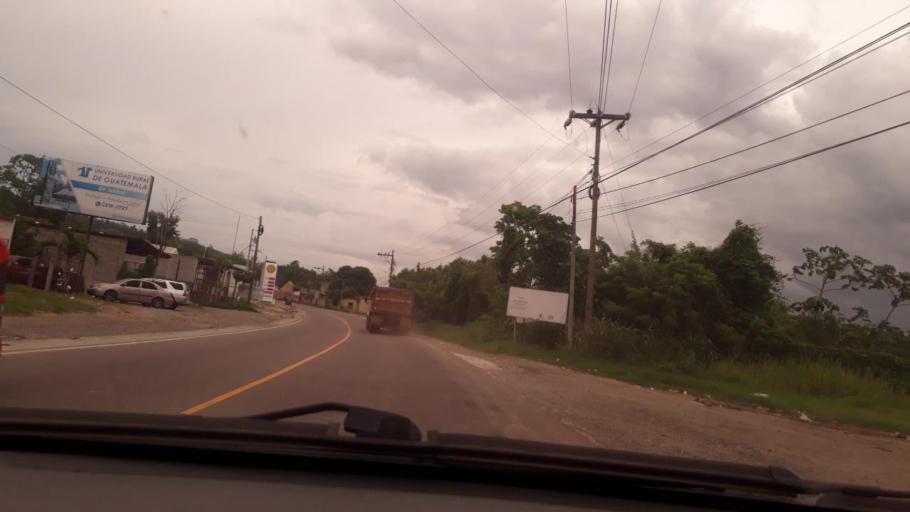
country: GT
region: Izabal
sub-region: Municipio de Los Amates
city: Los Amates
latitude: 15.2576
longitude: -89.0905
